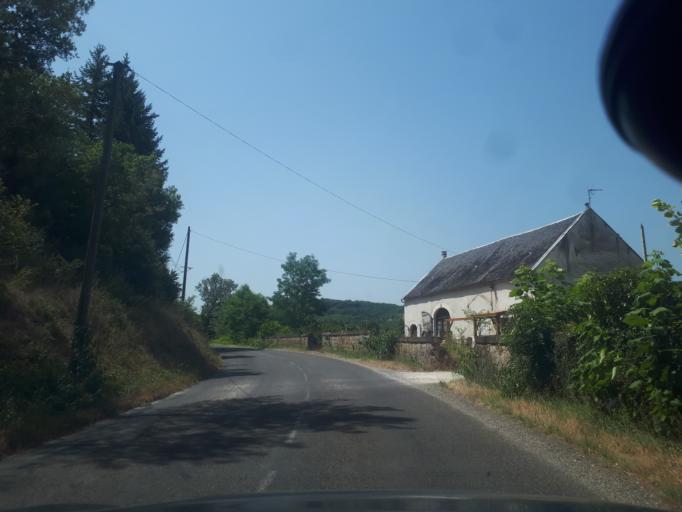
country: FR
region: Midi-Pyrenees
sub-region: Departement du Lot
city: Souillac
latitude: 44.8625
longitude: 1.4072
